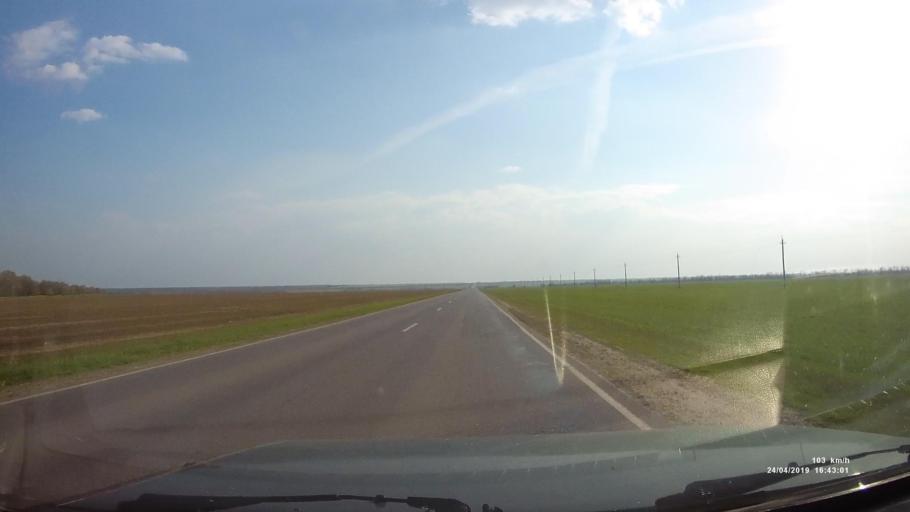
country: RU
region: Rostov
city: Gundorovskiy
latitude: 46.7997
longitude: 41.8460
